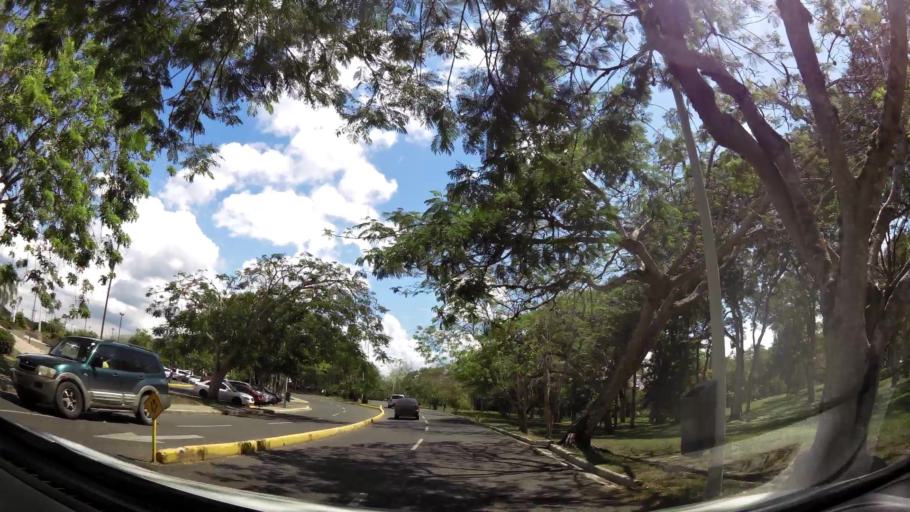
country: DO
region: Santiago
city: Santiago de los Caballeros
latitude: 19.4453
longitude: -70.6820
